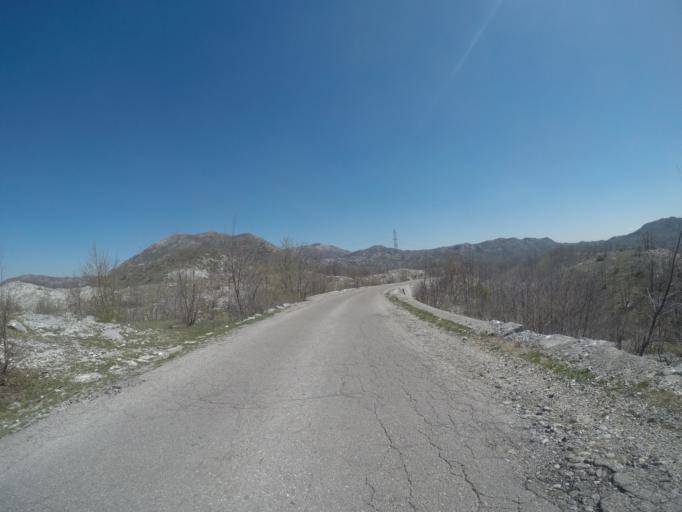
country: ME
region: Cetinje
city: Cetinje
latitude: 42.4402
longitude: 18.8732
